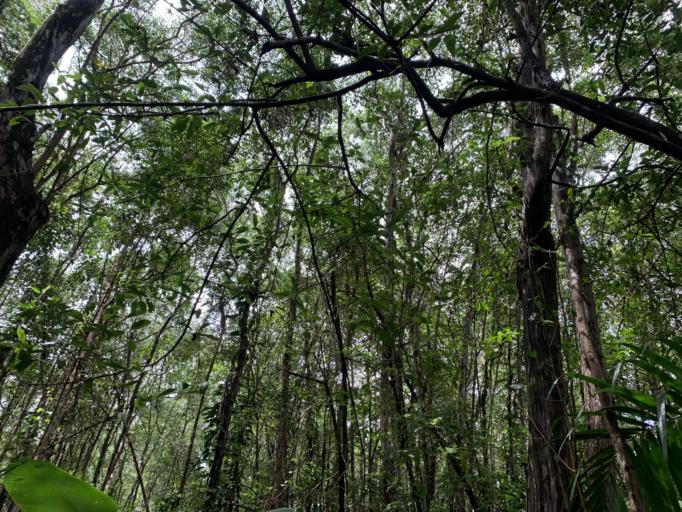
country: PA
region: Colon
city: Las Margaritas
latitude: 9.3202
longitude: -79.9146
